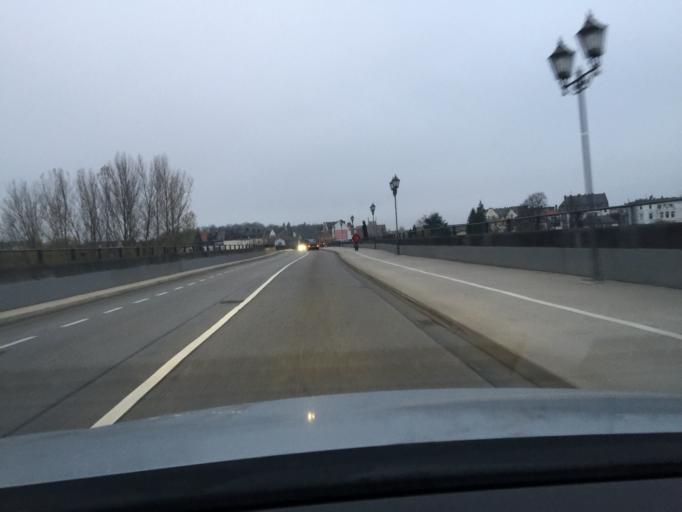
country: DE
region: Rheinland-Pfalz
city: Koblenz
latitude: 50.3631
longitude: 7.5933
